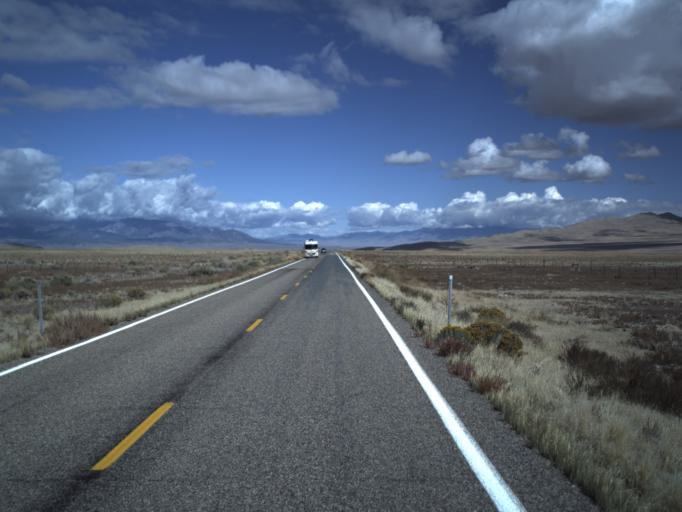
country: US
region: Utah
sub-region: Beaver County
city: Milford
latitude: 38.6682
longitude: -113.8827
